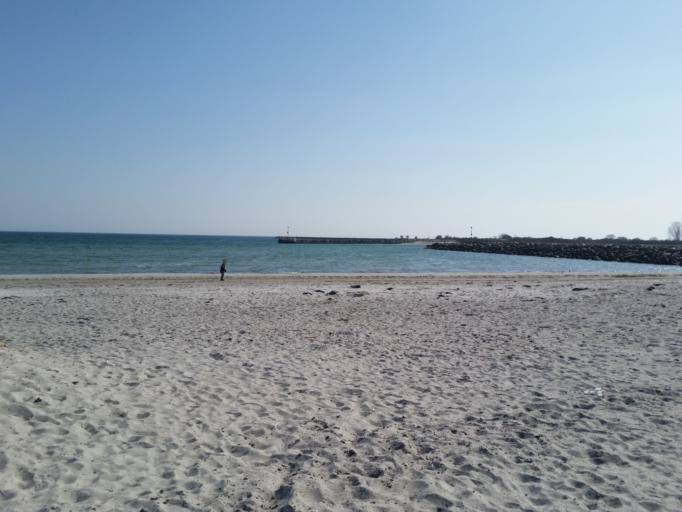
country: DK
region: Capital Region
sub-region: Brondby Kommune
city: Brondbyvester
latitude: 55.6118
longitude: 12.4011
